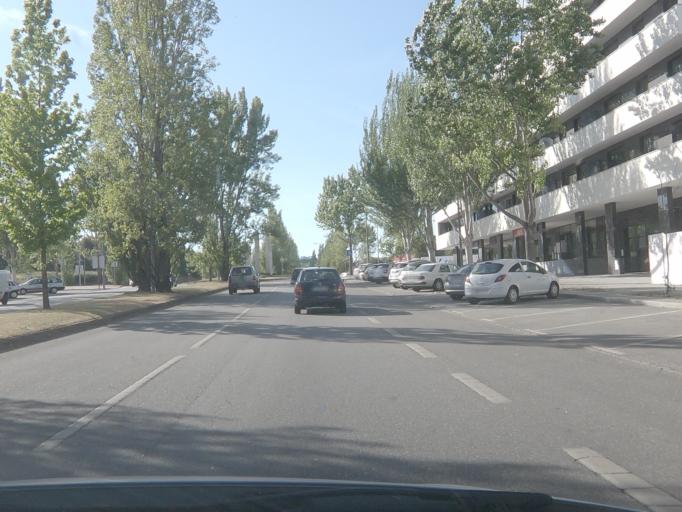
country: PT
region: Viseu
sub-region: Viseu
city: Viseu
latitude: 40.6673
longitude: -7.9175
